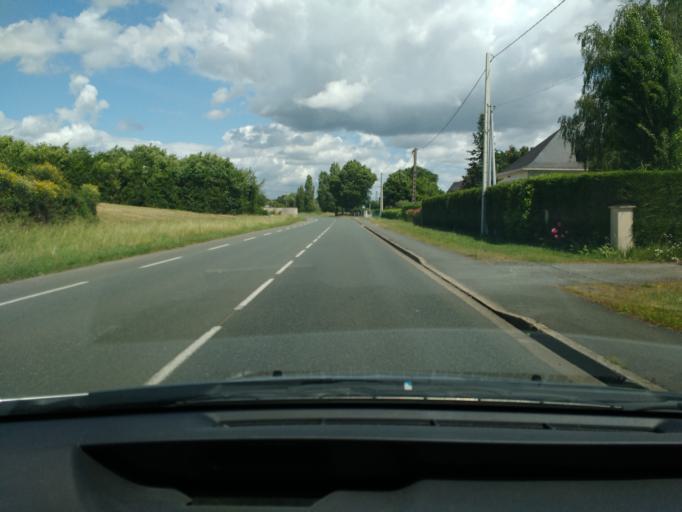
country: FR
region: Pays de la Loire
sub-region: Departement de Maine-et-Loire
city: Trelaze
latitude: 47.4837
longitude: -0.4859
